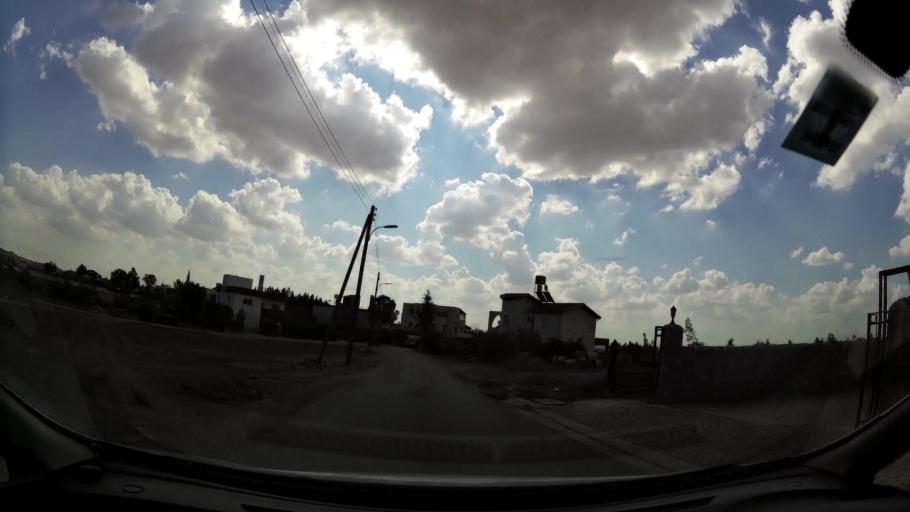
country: CY
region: Lefkosia
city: Nicosia
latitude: 35.2238
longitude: 33.3742
